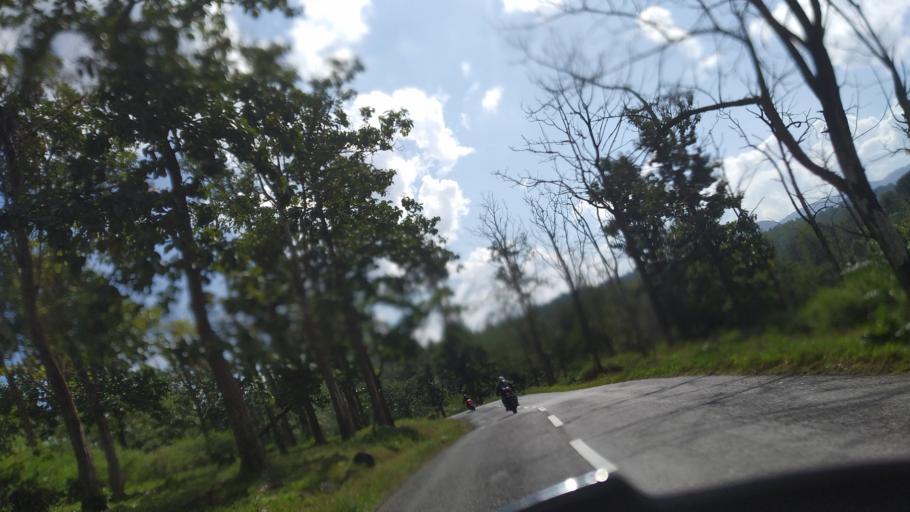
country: IN
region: Kerala
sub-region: Wayanad
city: Panamaram
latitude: 11.9150
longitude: 76.0632
